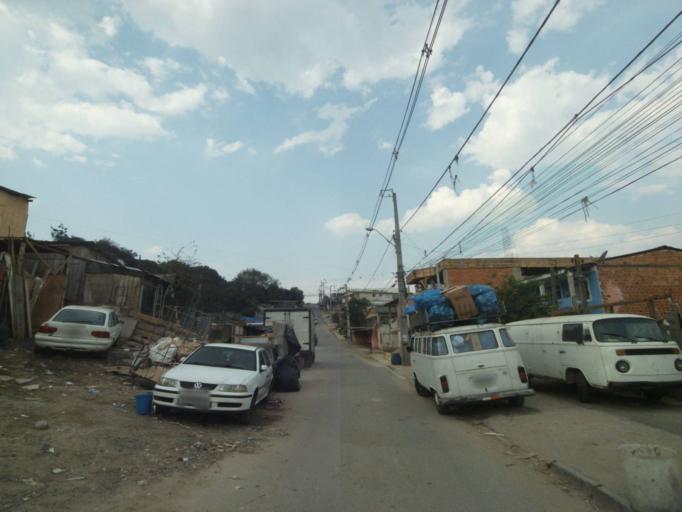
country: BR
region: Parana
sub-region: Curitiba
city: Curitiba
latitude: -25.4637
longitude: -49.2685
